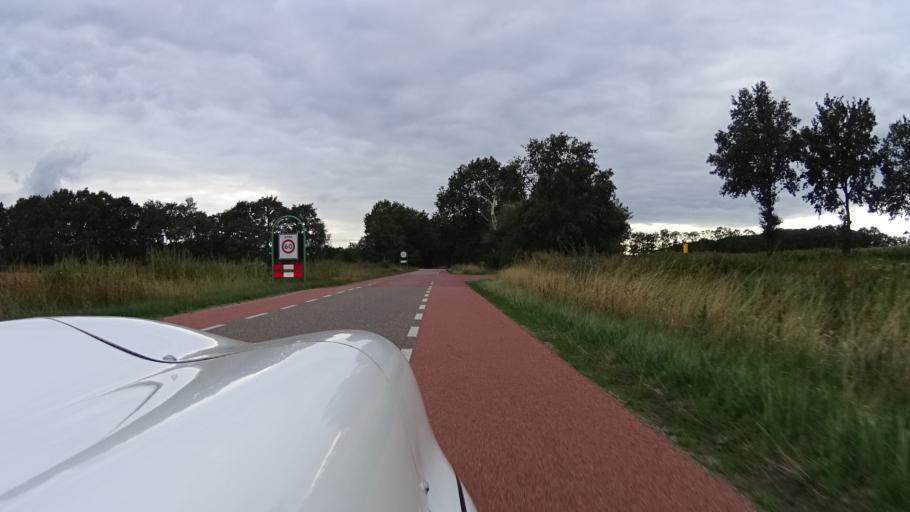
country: NL
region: North Brabant
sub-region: Gemeente Bernheze
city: Loosbroek
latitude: 51.6911
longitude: 5.4715
